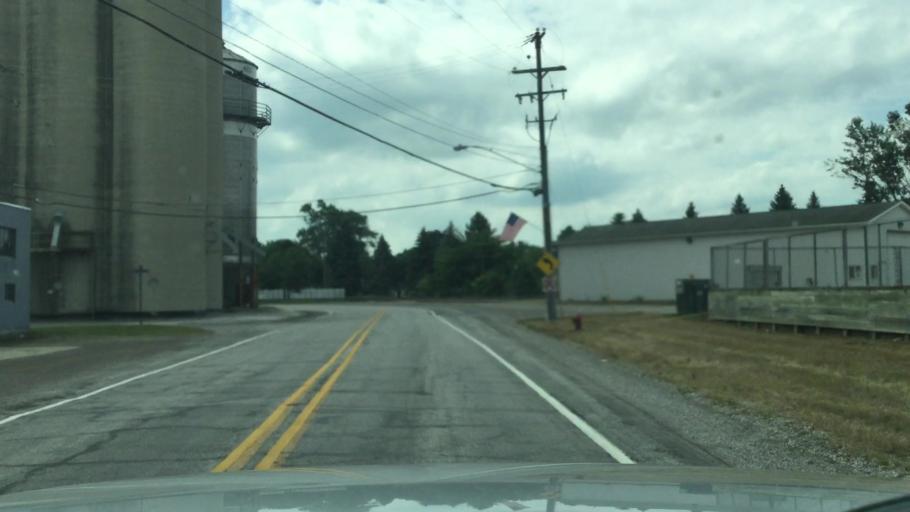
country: US
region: Michigan
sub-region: Saginaw County
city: Birch Run
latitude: 43.2519
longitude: -83.7944
